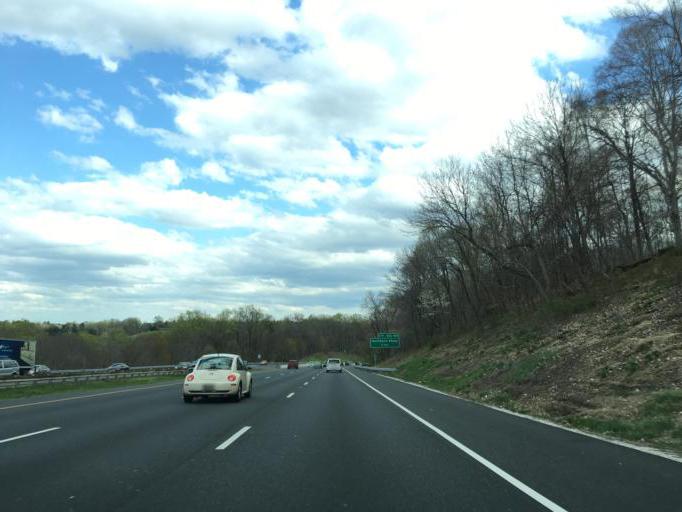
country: US
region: Maryland
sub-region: Baltimore County
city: Lutherville
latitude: 39.3767
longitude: -76.6575
